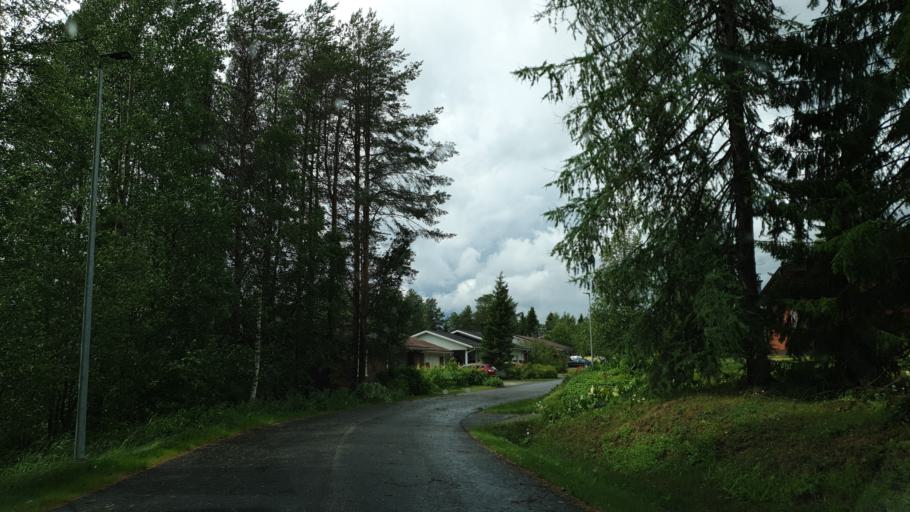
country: FI
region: Kainuu
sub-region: Kehys-Kainuu
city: Kuhmo
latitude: 64.1160
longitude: 29.5076
